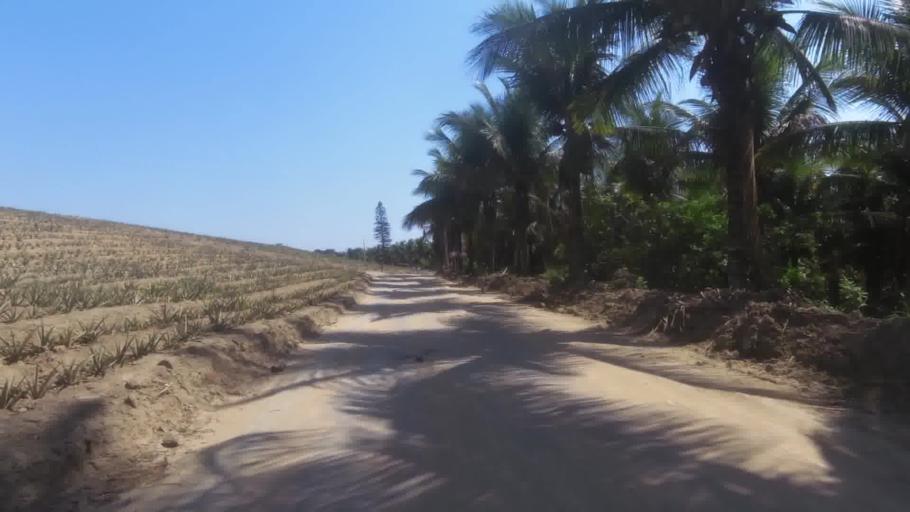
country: BR
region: Espirito Santo
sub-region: Marataizes
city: Marataizes
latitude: -21.1061
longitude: -40.8569
